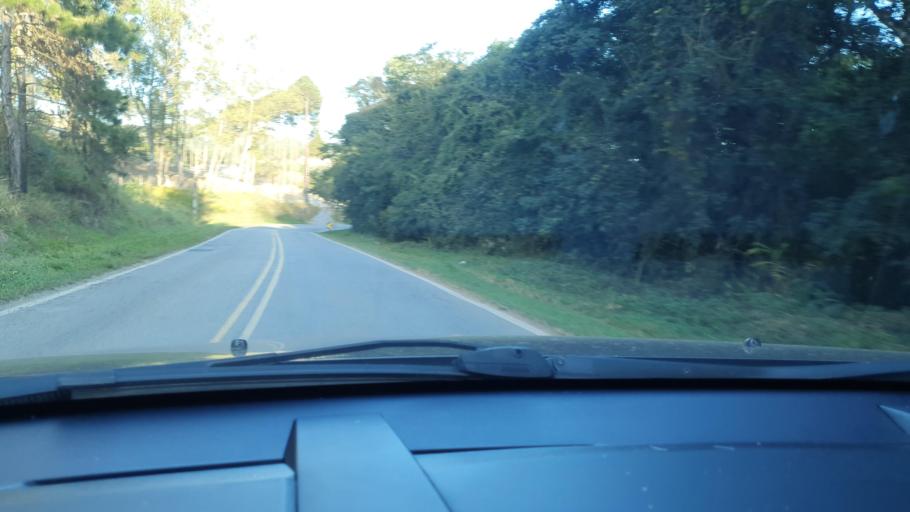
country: BR
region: Sao Paulo
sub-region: Piedade
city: Piedade
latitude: -23.6779
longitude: -47.3351
